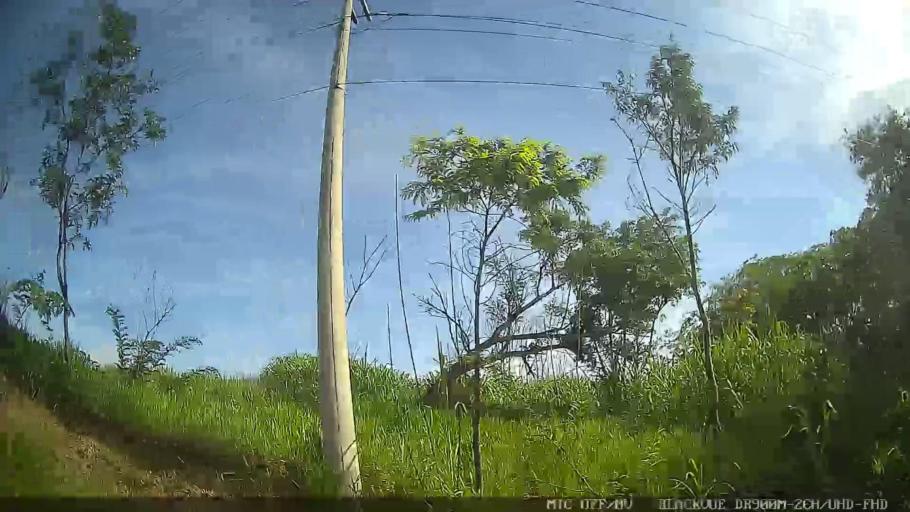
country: BR
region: Sao Paulo
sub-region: Jaguariuna
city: Jaguariuna
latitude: -22.6693
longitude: -47.0771
